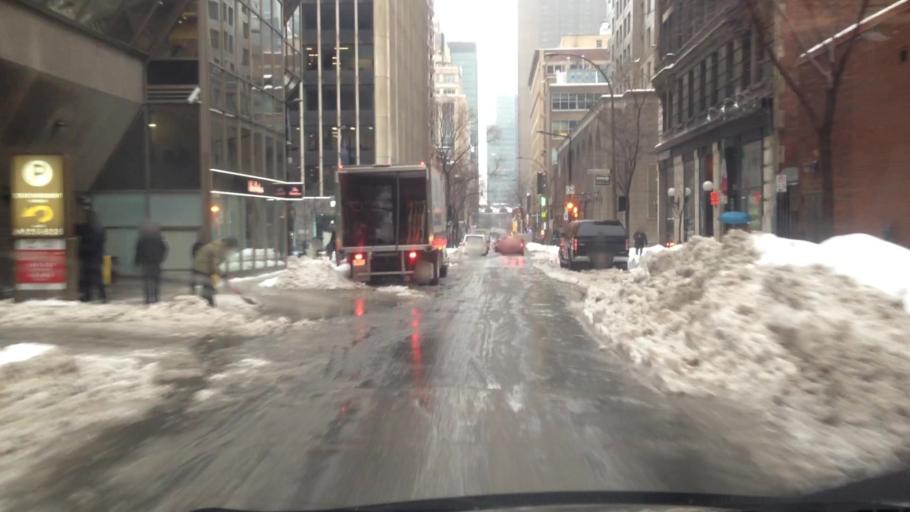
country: CA
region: Quebec
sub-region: Montreal
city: Montreal
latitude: 45.5006
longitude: -73.5761
